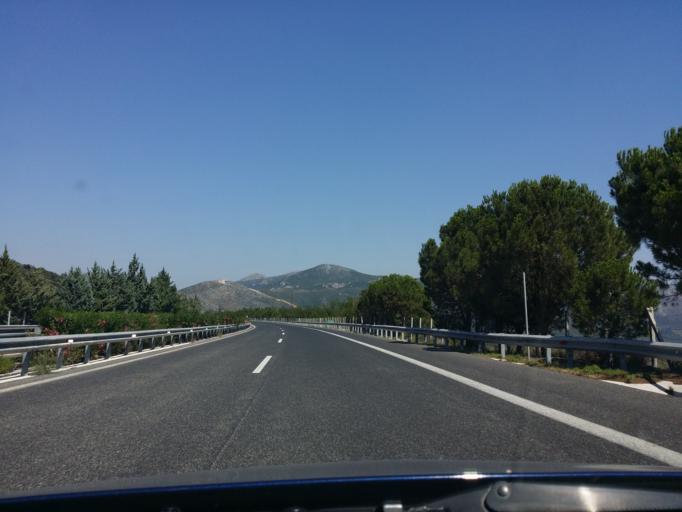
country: GR
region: Peloponnese
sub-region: Nomos Korinthias
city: Nemea
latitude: 37.7830
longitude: 22.6967
